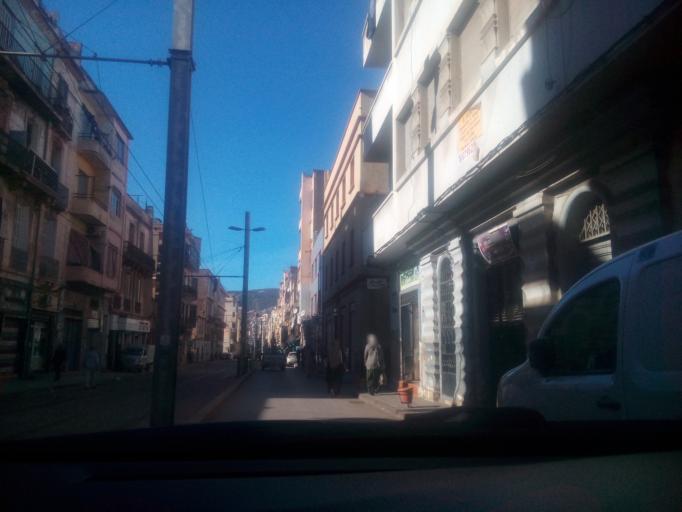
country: DZ
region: Oran
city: Oran
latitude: 35.6998
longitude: -0.6395
